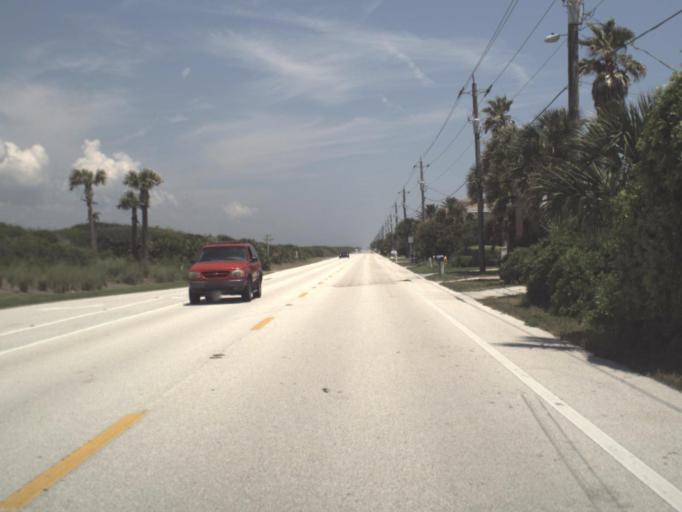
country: US
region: Florida
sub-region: Saint Johns County
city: Villano Beach
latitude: 29.9934
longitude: -81.3160
